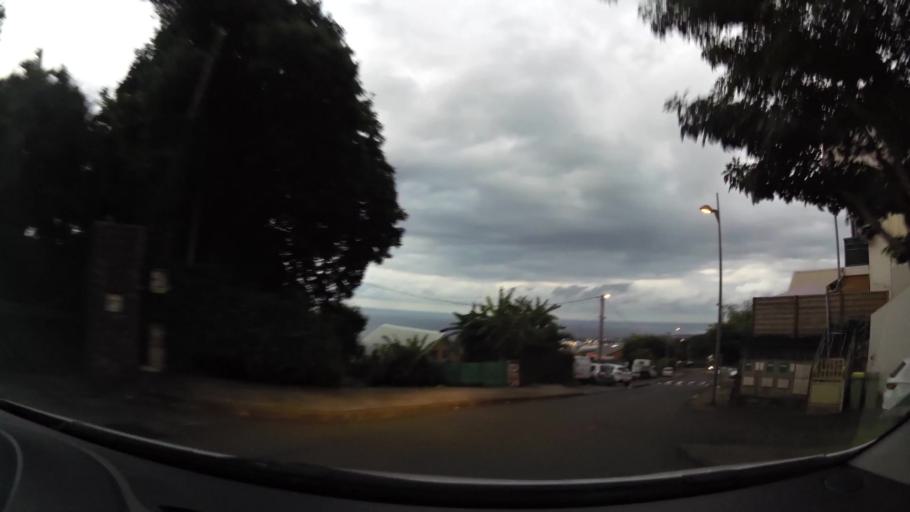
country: RE
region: Reunion
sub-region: Reunion
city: Saint-Denis
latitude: -20.9087
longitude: 55.4648
